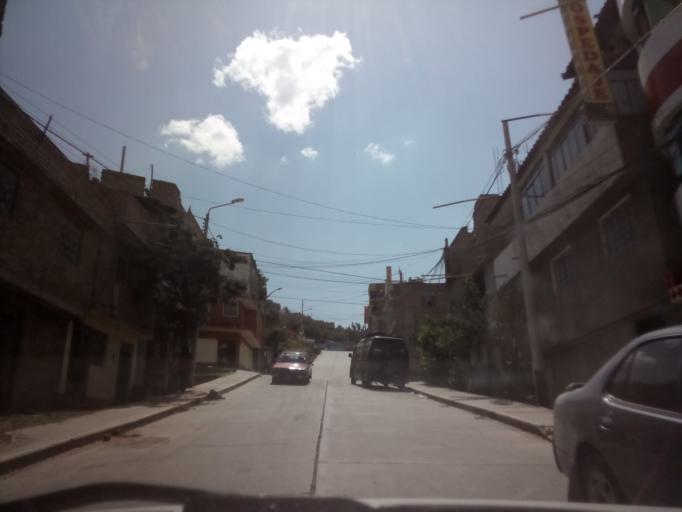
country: PE
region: Ayacucho
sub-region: Provincia de Huamanga
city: Ayacucho
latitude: -13.1478
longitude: -74.2309
